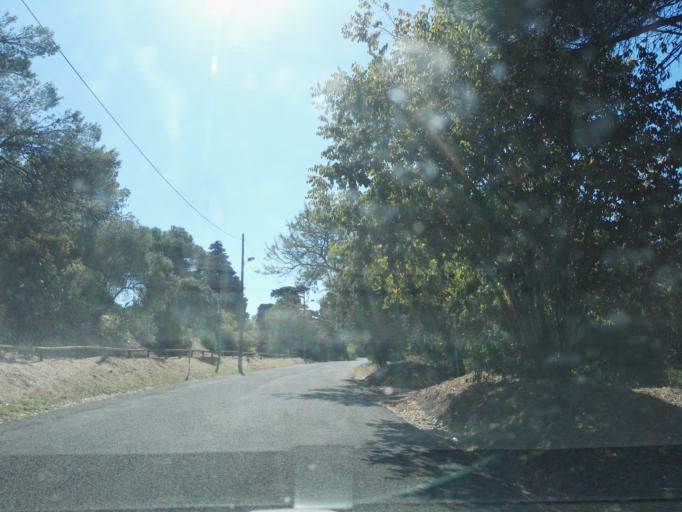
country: PT
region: Lisbon
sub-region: Oeiras
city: Alges
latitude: 38.7202
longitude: -9.1999
